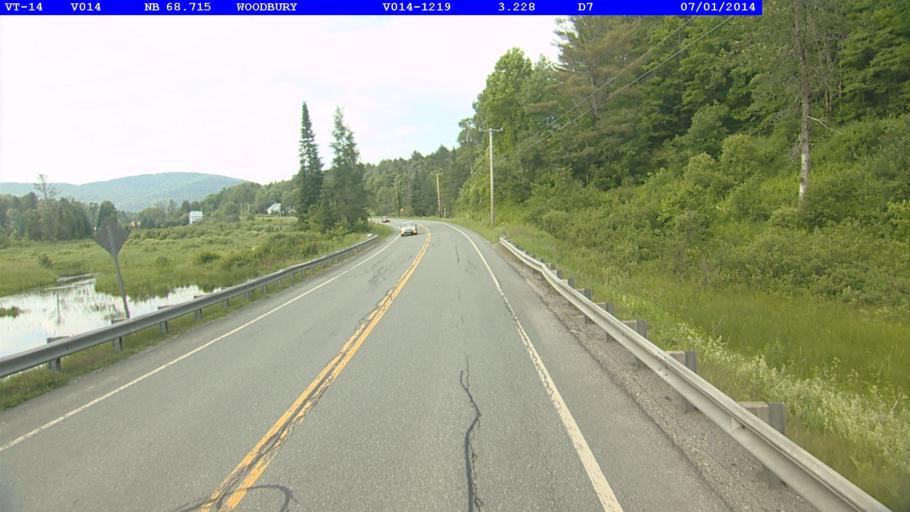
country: US
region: Vermont
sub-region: Caledonia County
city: Hardwick
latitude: 44.4347
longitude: -72.4132
